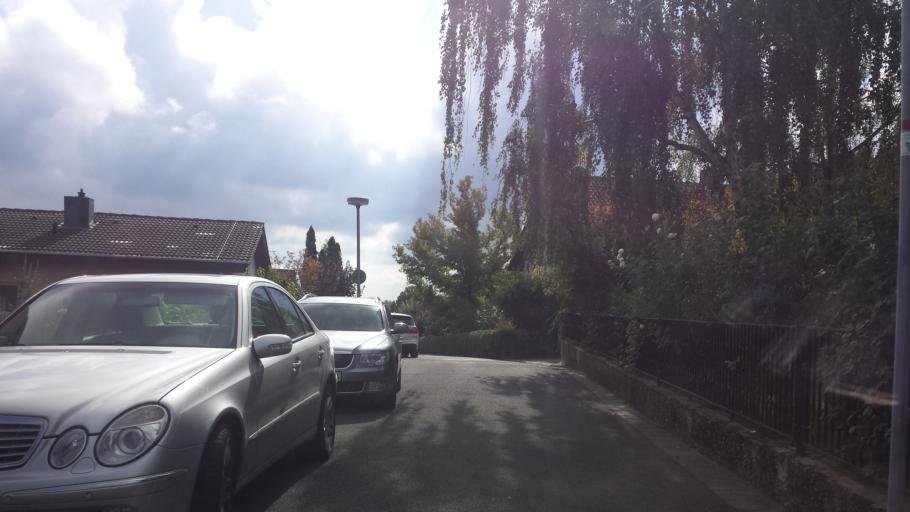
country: DE
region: Rheinland-Pfalz
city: Wachenheim
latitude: 49.4365
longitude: 8.1760
